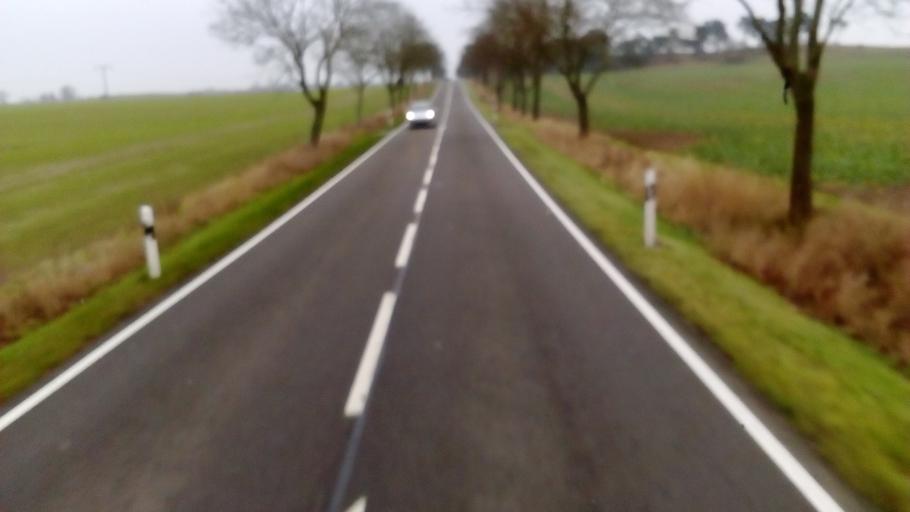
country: DE
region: Brandenburg
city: Goritz
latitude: 53.4928
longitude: 13.8844
